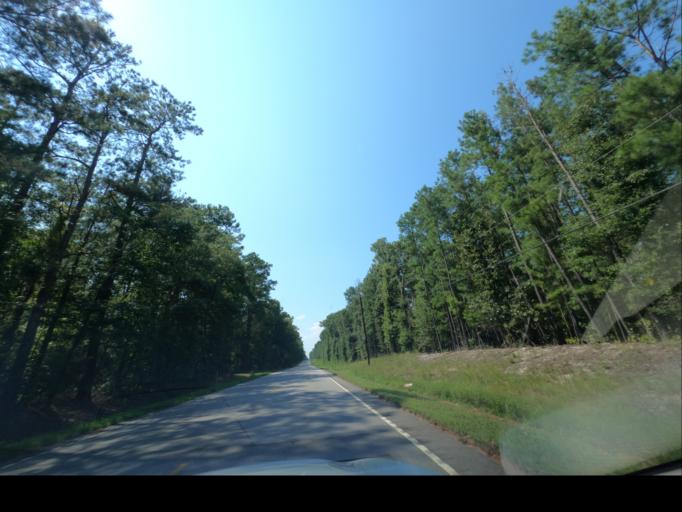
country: US
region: South Carolina
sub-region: Richland County
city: Hopkins
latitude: 33.9117
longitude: -80.9405
